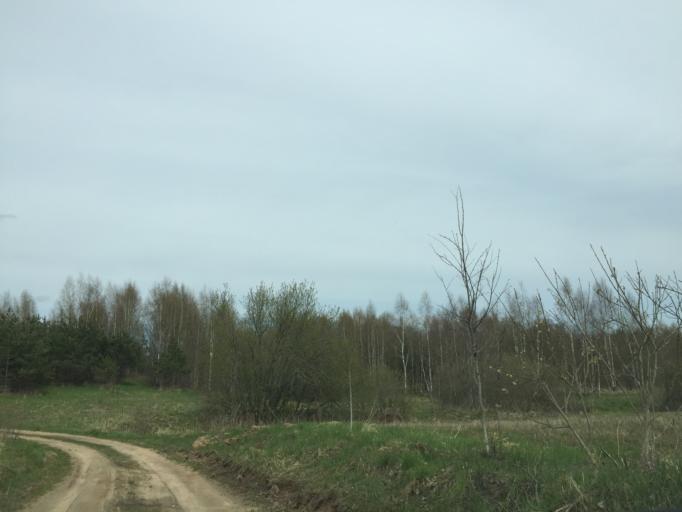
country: LV
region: Ludzas Rajons
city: Ludza
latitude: 56.5271
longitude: 27.5830
